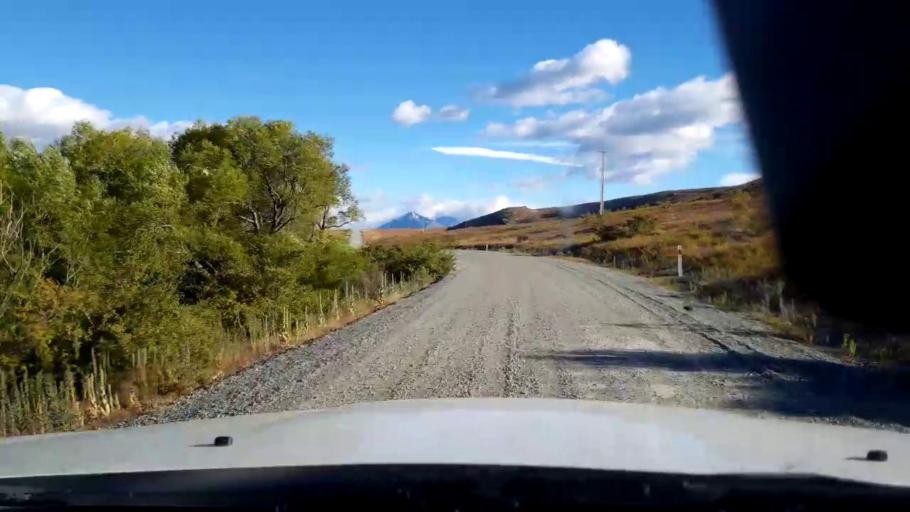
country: NZ
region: Canterbury
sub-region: Timaru District
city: Pleasant Point
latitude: -43.9269
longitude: 170.5605
